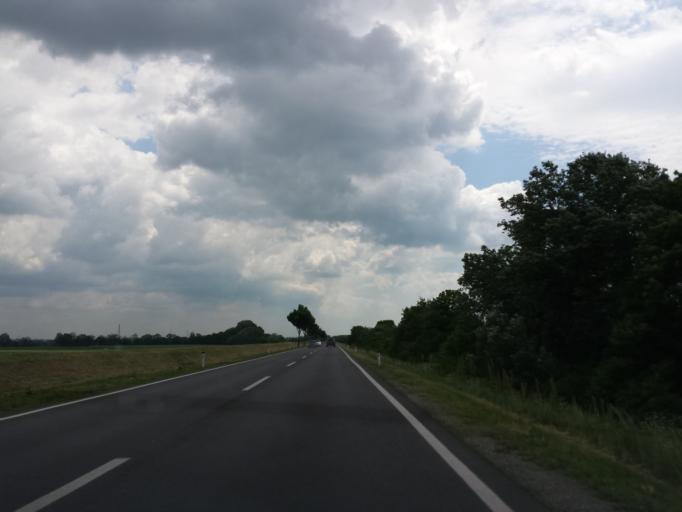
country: AT
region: Lower Austria
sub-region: Politischer Bezirk Bruck an der Leitha
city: Berg
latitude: 48.1245
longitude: 17.0375
